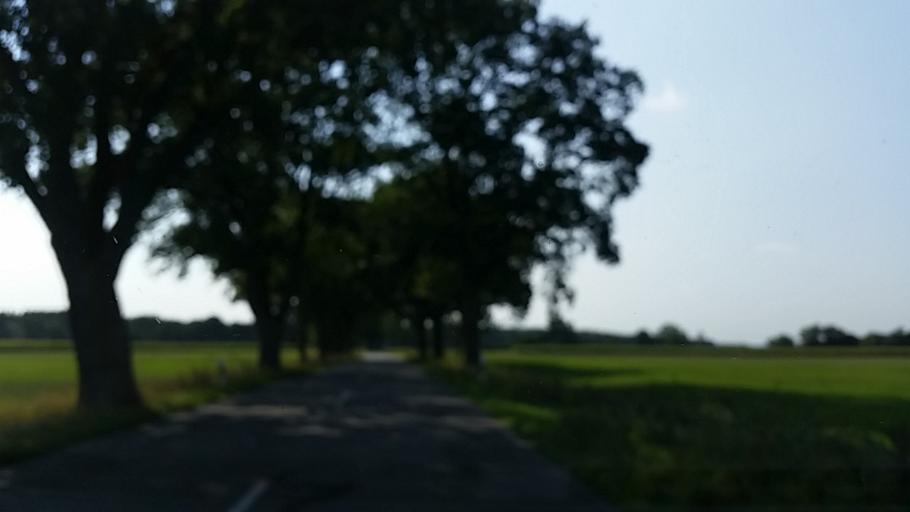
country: DE
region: Lower Saxony
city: Langendorf
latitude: 53.1157
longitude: 11.2366
